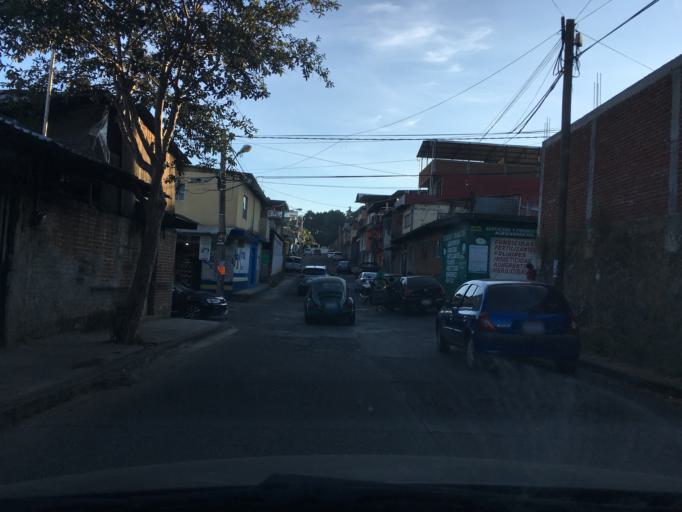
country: MX
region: Michoacan
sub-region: Uruapan
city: Uruapan
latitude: 19.4145
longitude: -102.0671
